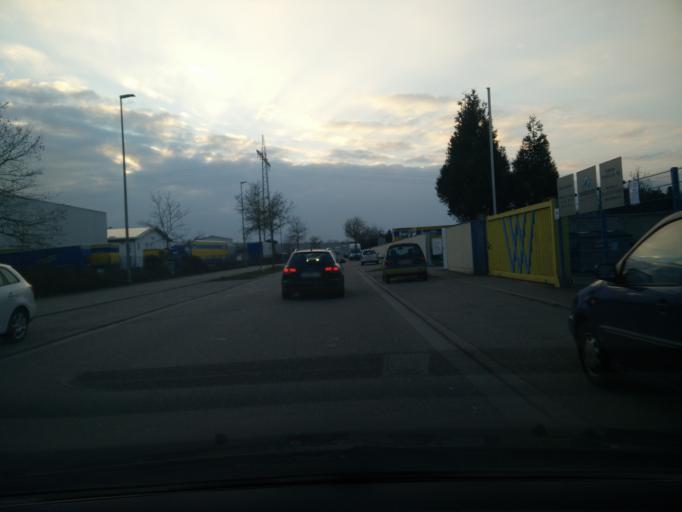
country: DE
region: Rheinland-Pfalz
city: Kandel
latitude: 49.0989
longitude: 8.1760
